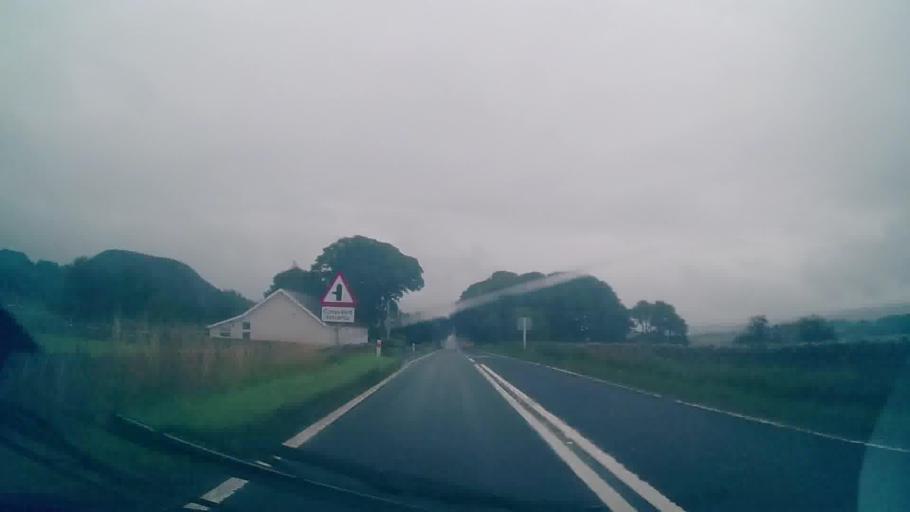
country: GB
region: Scotland
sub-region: Dumfries and Galloway
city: Sanquhar
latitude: 55.3799
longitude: -3.9573
